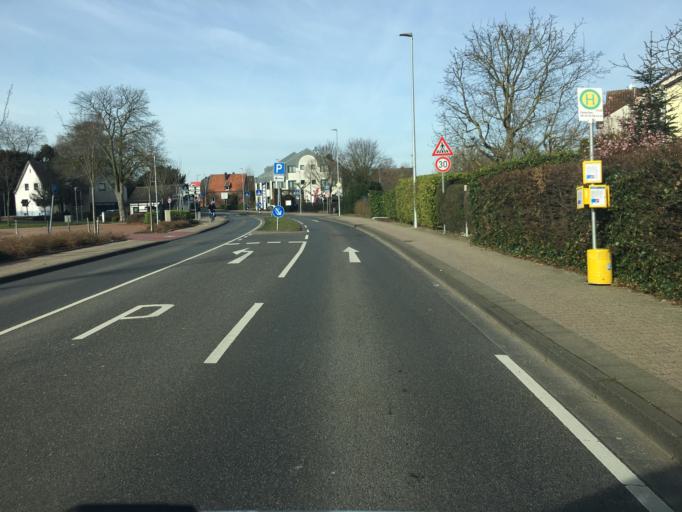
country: DE
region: North Rhine-Westphalia
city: Erkelenz
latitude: 51.0821
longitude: 6.3170
